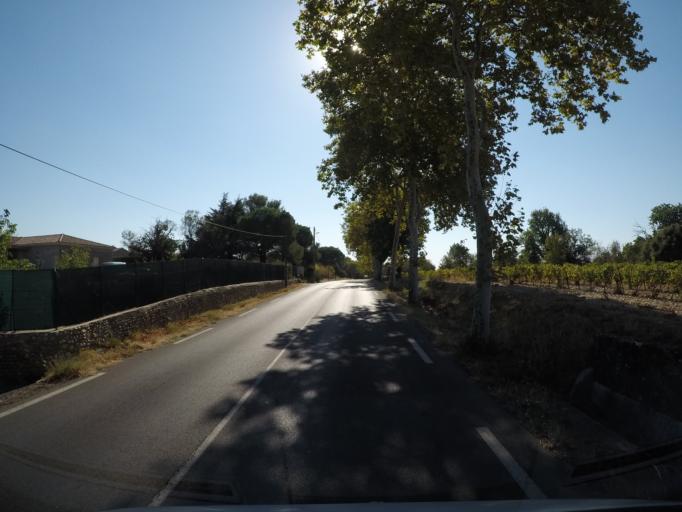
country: FR
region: Languedoc-Roussillon
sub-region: Departement du Gard
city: Boisset-et-Gaujac
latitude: 44.0325
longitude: 4.0101
